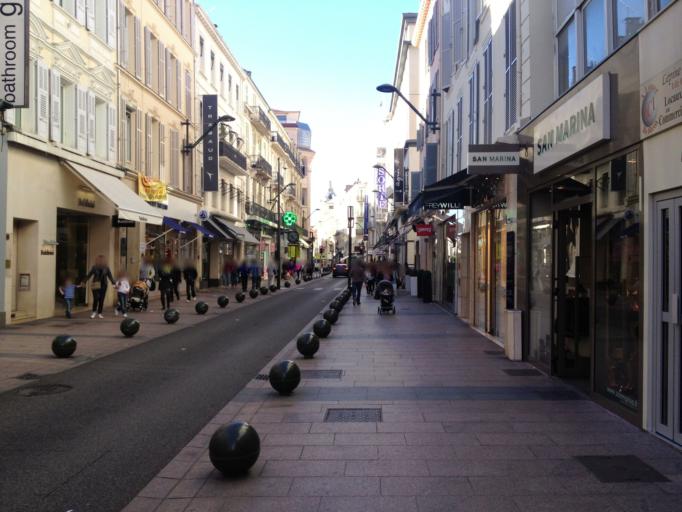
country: FR
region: Provence-Alpes-Cote d'Azur
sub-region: Departement des Alpes-Maritimes
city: Cannes
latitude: 43.5527
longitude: 7.0203
